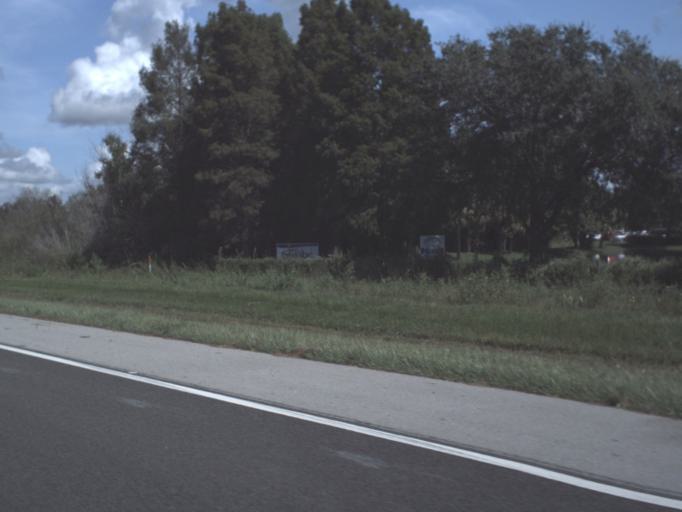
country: US
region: Florida
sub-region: Sarasota County
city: Nokomis
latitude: 27.1413
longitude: -82.4102
